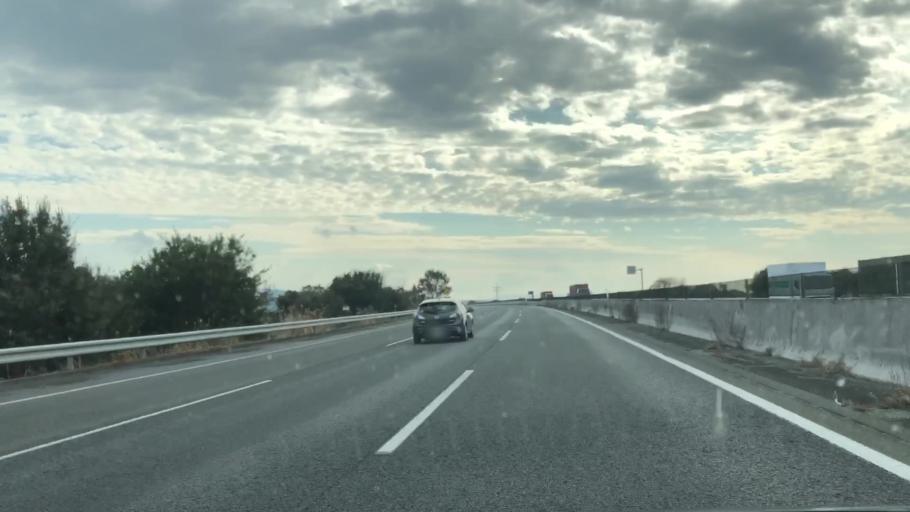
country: JP
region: Saga Prefecture
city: Tosu
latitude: 33.3498
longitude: 130.5376
